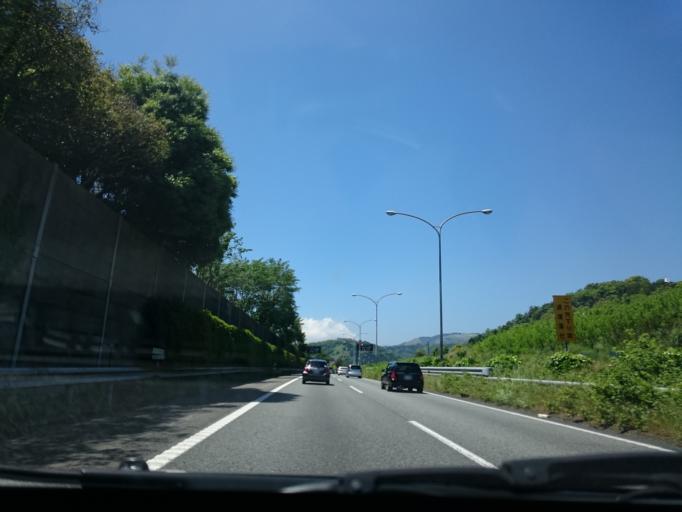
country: JP
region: Kanagawa
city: Hadano
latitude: 35.3544
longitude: 139.1184
